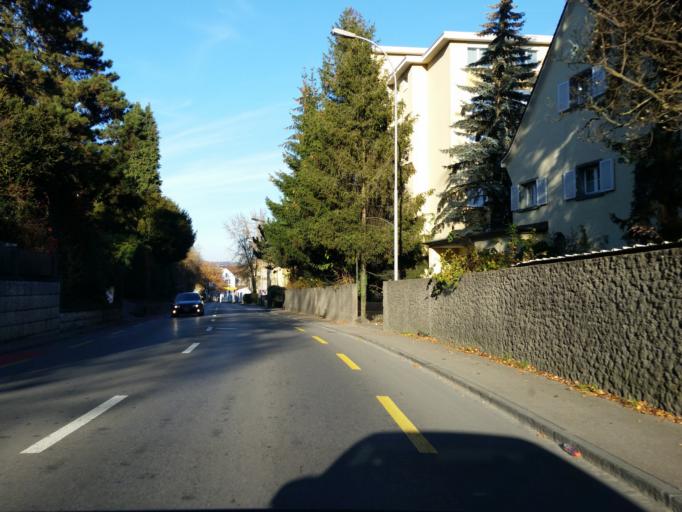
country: CH
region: Schaffhausen
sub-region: Bezirk Schaffhausen
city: Neuhausen
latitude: 47.6840
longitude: 8.6197
